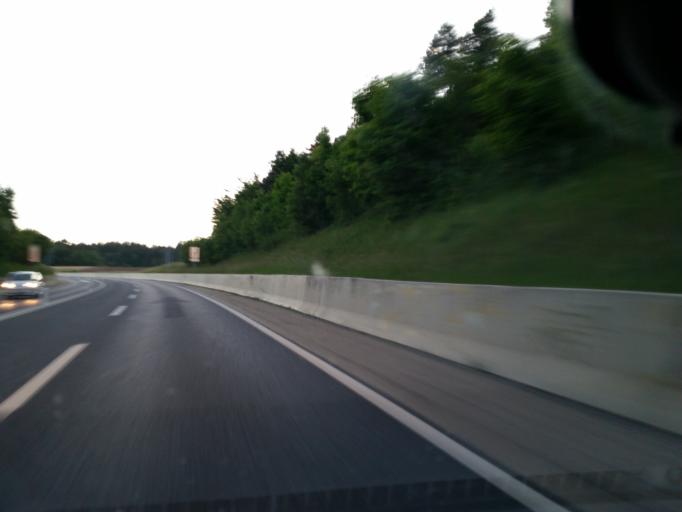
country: CH
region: Vaud
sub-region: Jura-Nord vaudois District
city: Orbe
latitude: 46.7406
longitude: 6.5126
